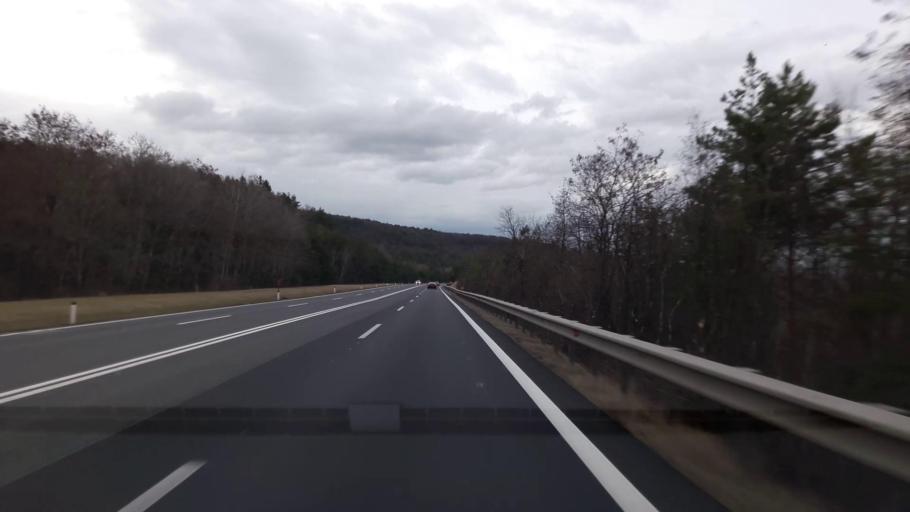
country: AT
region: Burgenland
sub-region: Politischer Bezirk Mattersburg
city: Sieggraben
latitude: 47.6921
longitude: 16.3819
